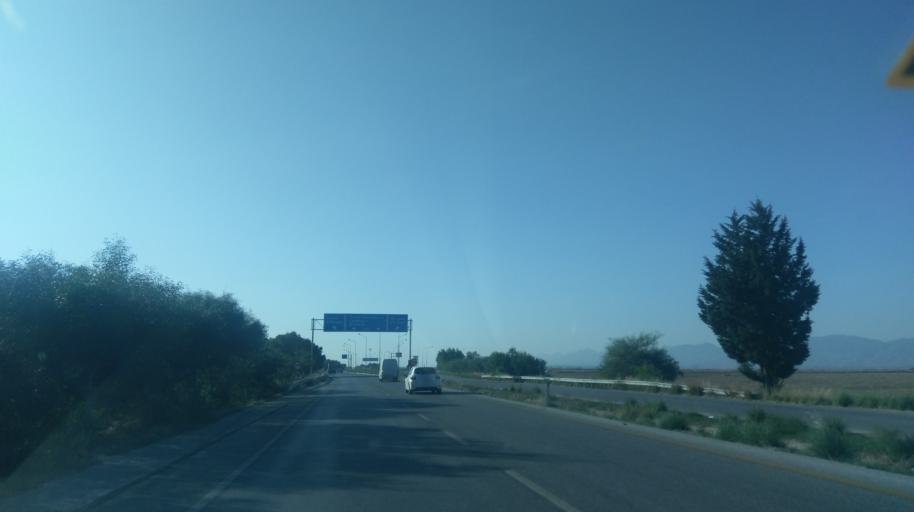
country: CY
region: Ammochostos
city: Lefkonoiko
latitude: 35.1825
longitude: 33.7045
